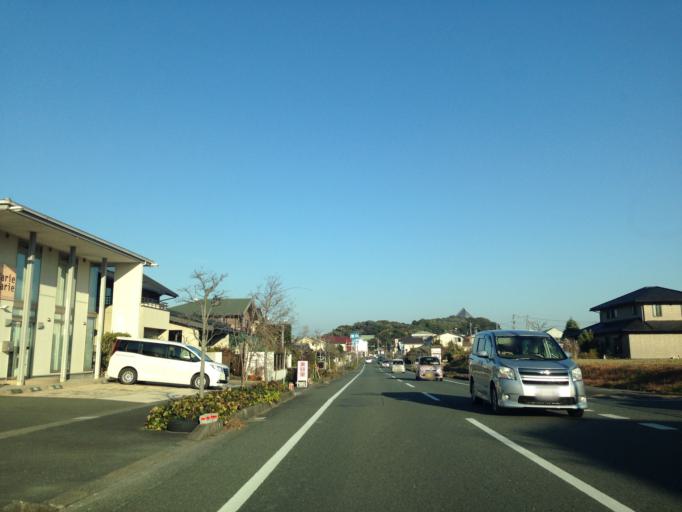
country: JP
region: Shizuoka
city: Kakegawa
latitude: 34.7672
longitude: 137.9906
